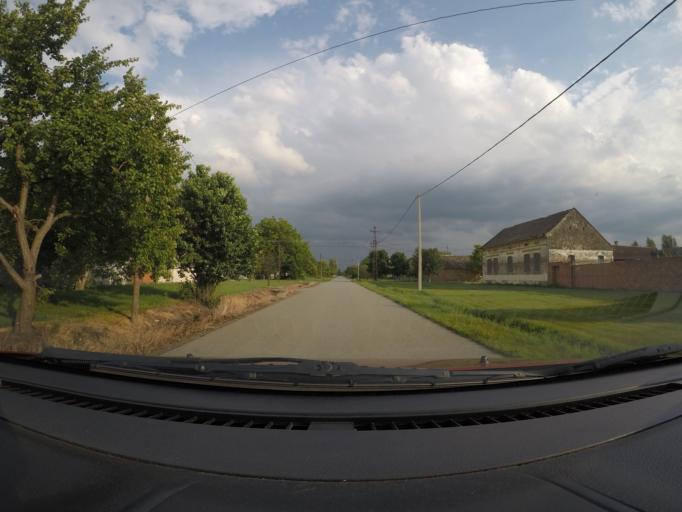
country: RS
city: Debeljaca
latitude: 45.0750
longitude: 20.5996
